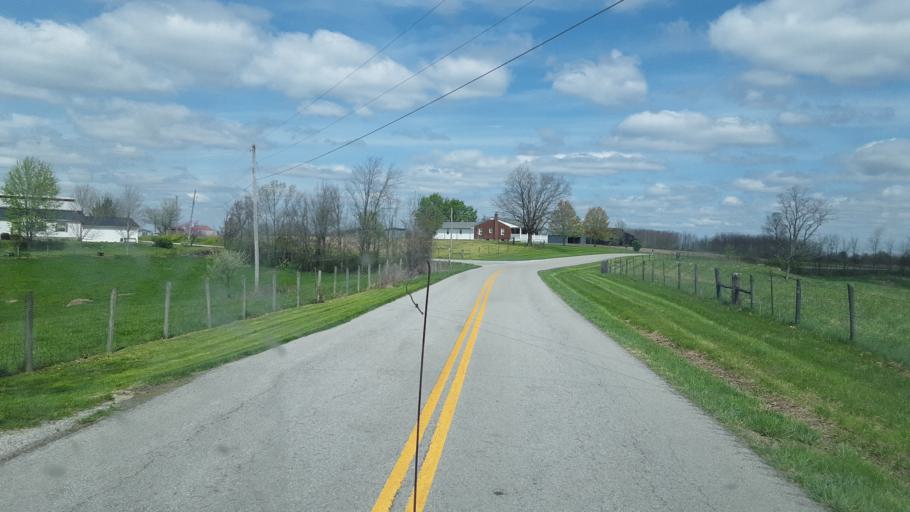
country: US
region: Kentucky
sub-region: Owen County
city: Owenton
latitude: 38.6221
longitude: -84.7862
